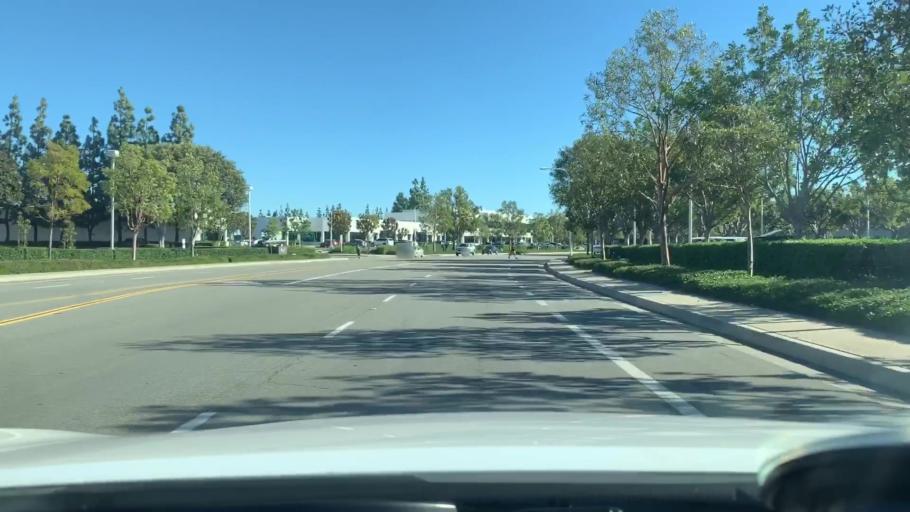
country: US
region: California
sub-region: Orange County
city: Laguna Woods
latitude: 33.6641
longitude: -117.7453
